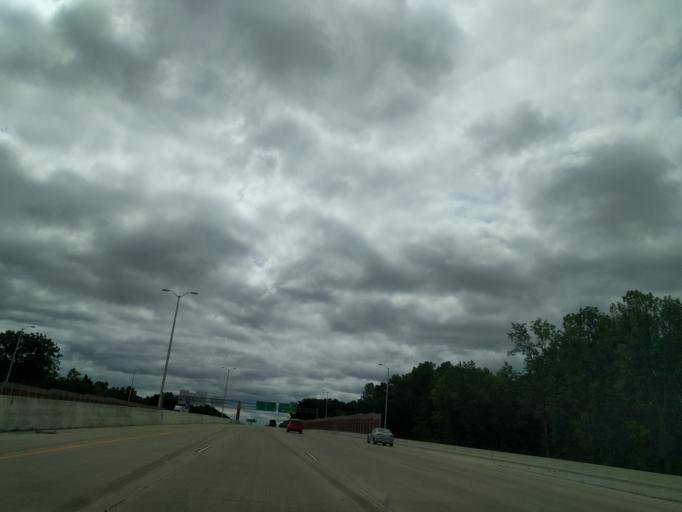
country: US
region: Wisconsin
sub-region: Brown County
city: Howard
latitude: 44.5219
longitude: -88.0823
